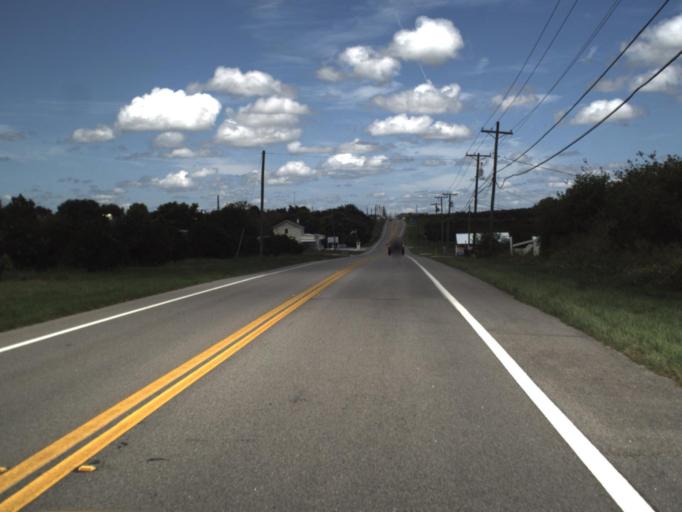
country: US
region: Florida
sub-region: Polk County
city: Dundee
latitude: 27.9704
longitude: -81.5948
